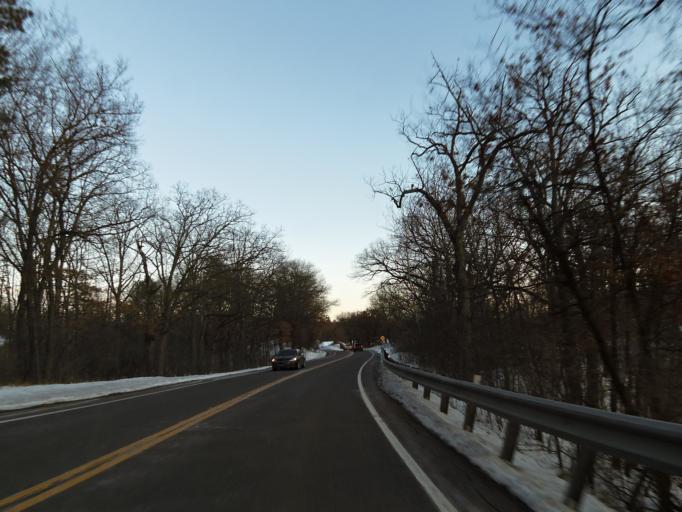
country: US
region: Minnesota
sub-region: Washington County
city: Dellwood
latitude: 45.0897
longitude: -92.9577
